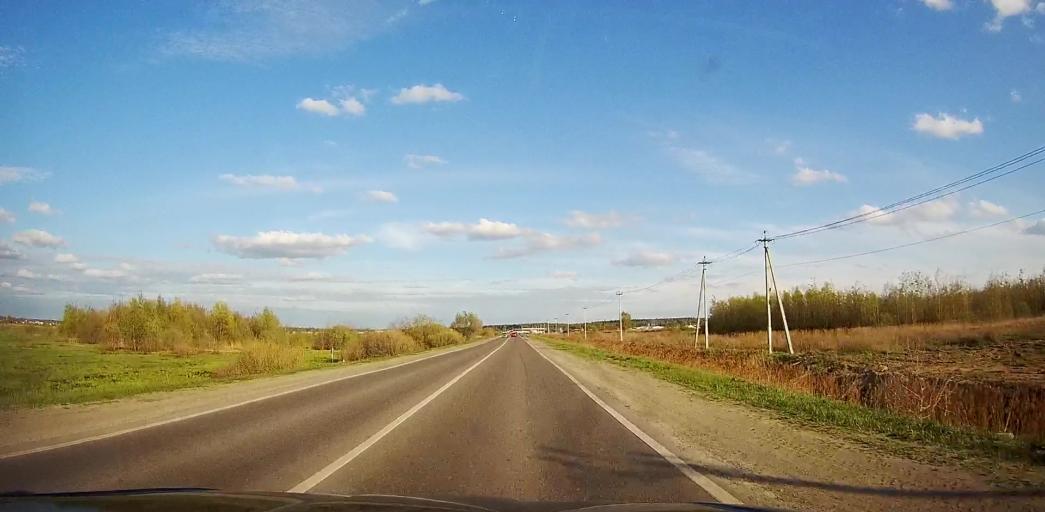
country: RU
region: Moskovskaya
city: Malyshevo
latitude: 55.4920
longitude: 38.3150
